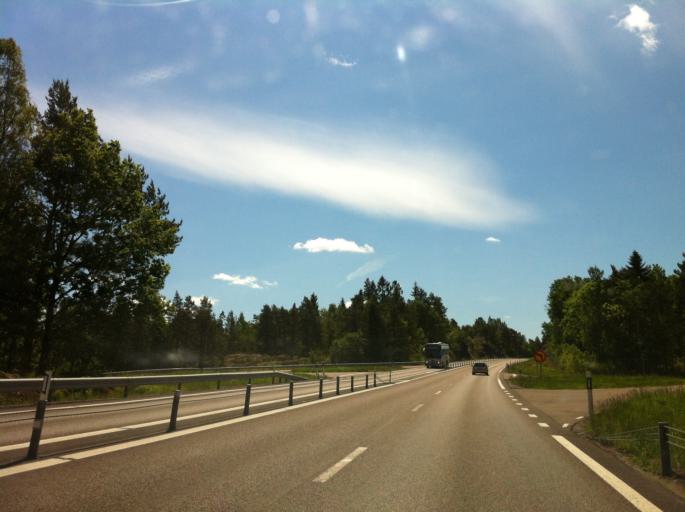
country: SE
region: Vaestra Goetaland
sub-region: Melleruds Kommun
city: Mellerud
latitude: 58.7642
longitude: 12.4895
